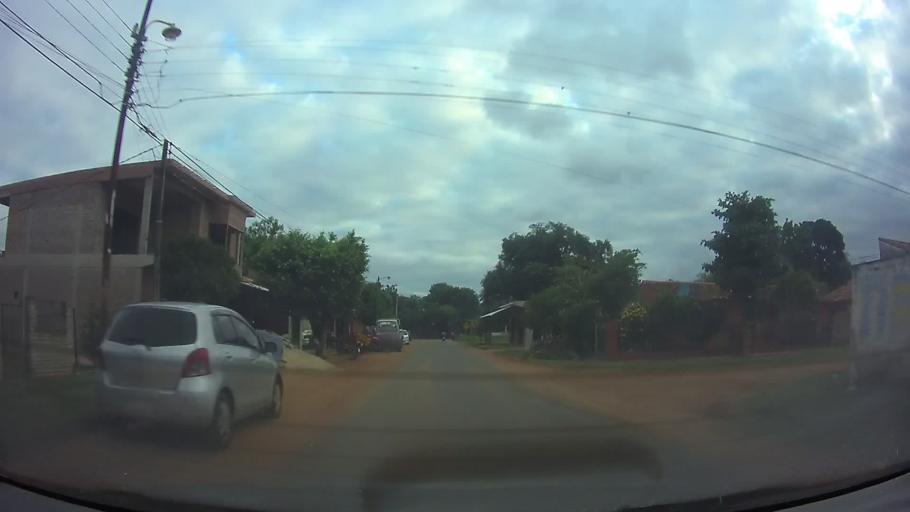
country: PY
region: Central
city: San Lorenzo
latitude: -25.2858
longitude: -57.4869
